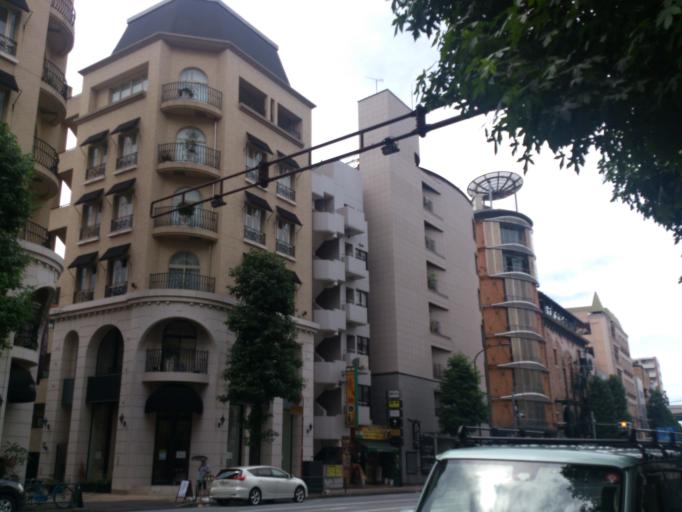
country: JP
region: Tokyo
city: Tokyo
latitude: 35.6574
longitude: 139.7240
